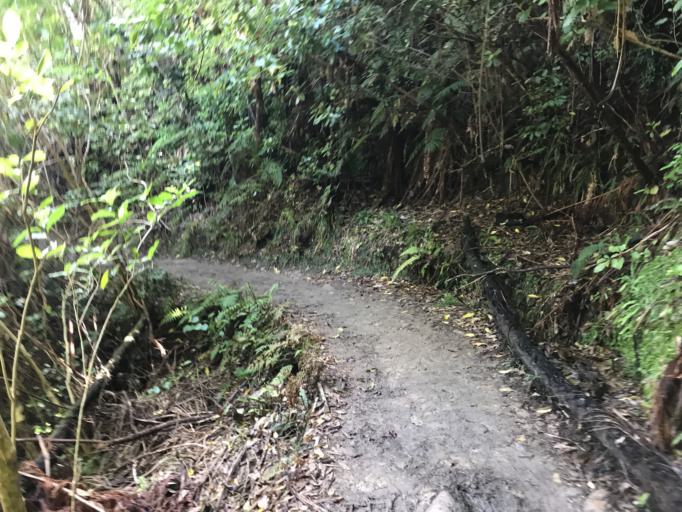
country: NZ
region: Marlborough
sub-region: Marlborough District
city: Picton
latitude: -41.2584
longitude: 173.9351
